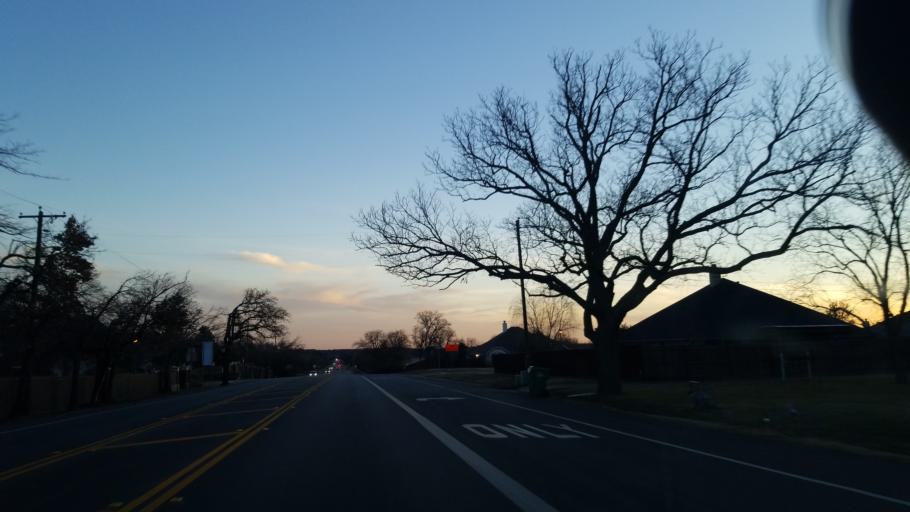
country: US
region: Texas
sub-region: Denton County
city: Denton
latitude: 33.1731
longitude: -97.1420
